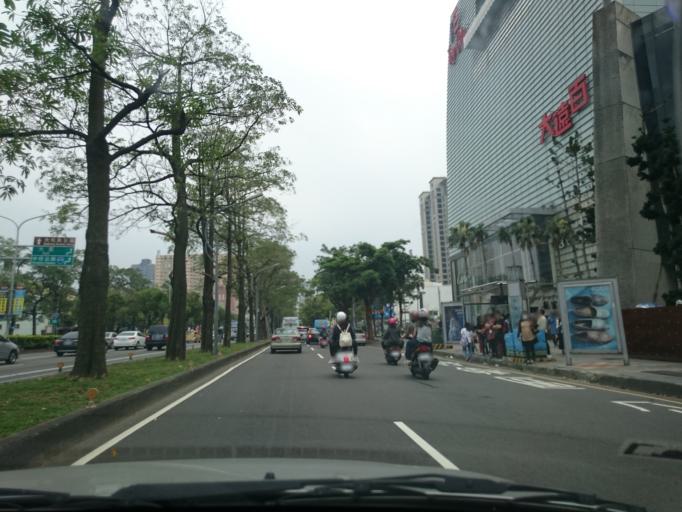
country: TW
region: Taiwan
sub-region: Taichung City
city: Taichung
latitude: 24.1655
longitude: 120.6441
